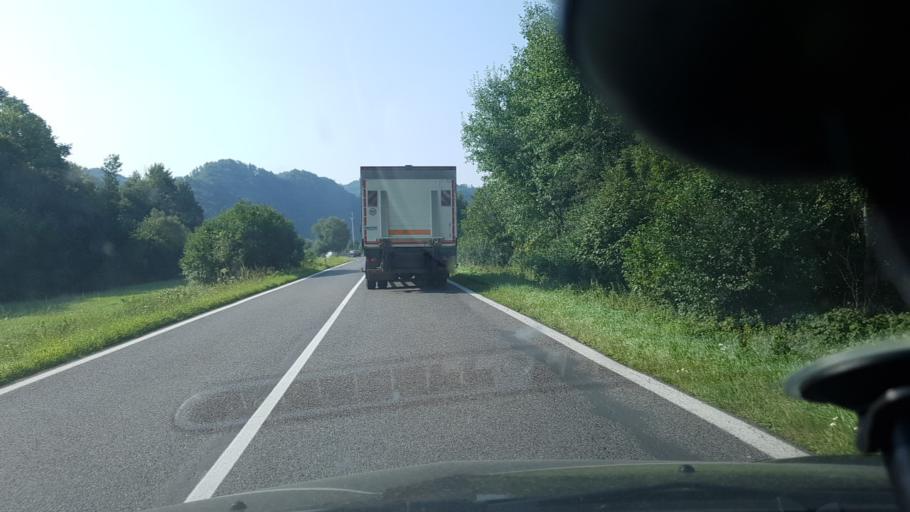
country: SK
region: Zilinsky
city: Tvrdosin
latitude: 49.2781
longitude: 19.4620
